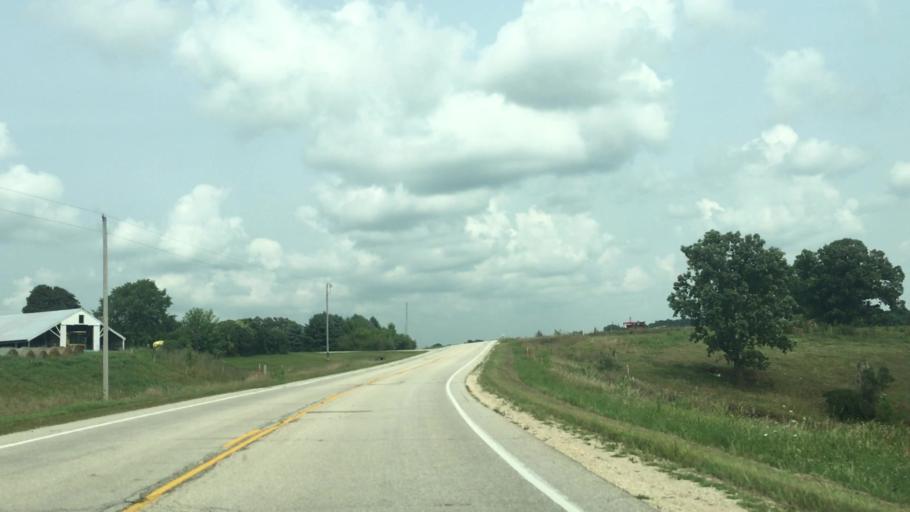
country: US
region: Minnesota
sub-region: Fillmore County
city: Preston
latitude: 43.6817
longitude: -91.9424
